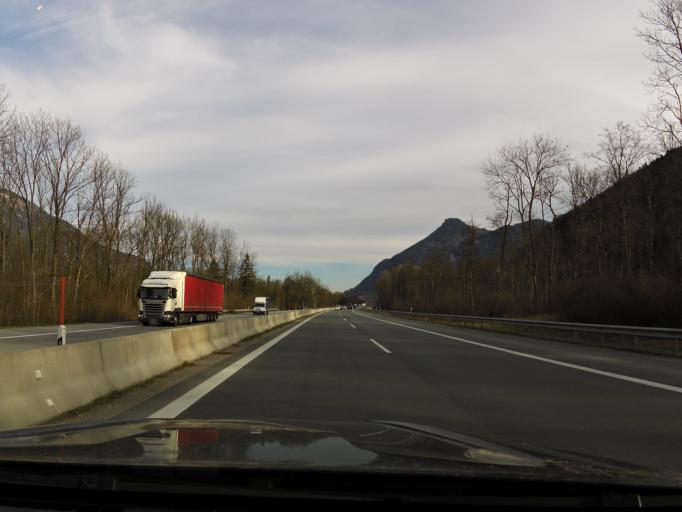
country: DE
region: Bavaria
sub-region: Upper Bavaria
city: Oberaudorf
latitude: 47.6558
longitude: 12.1849
